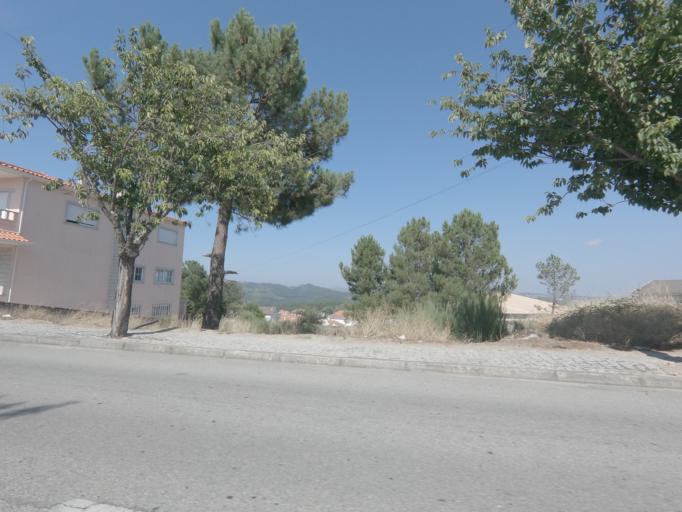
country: PT
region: Viseu
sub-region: Moimenta da Beira
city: Moimenta da Beira
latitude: 40.9810
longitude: -7.6180
